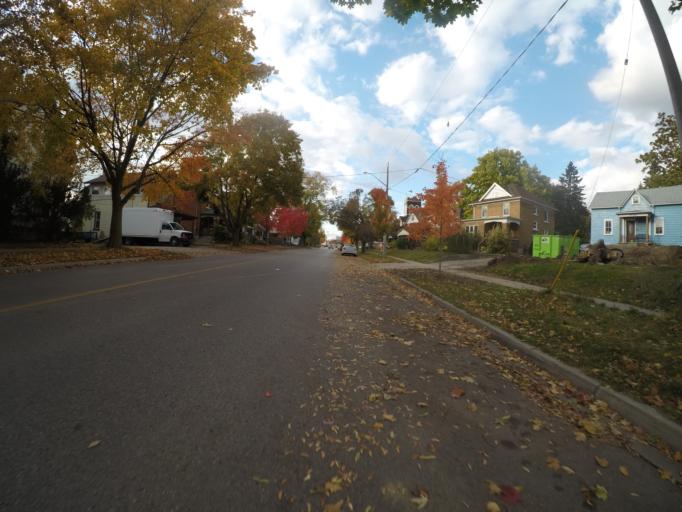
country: CA
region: Ontario
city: Waterloo
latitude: 43.4531
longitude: -80.5089
